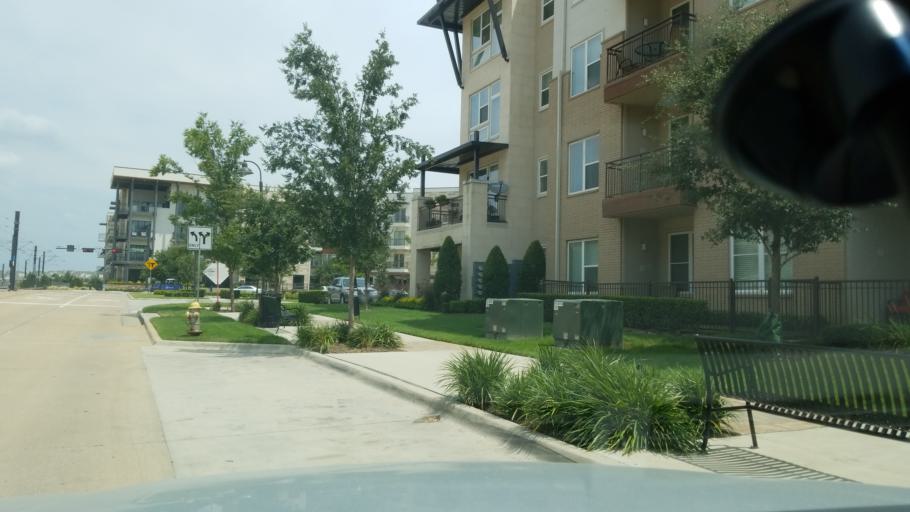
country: US
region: Texas
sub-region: Dallas County
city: Irving
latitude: 32.8732
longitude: -96.9354
